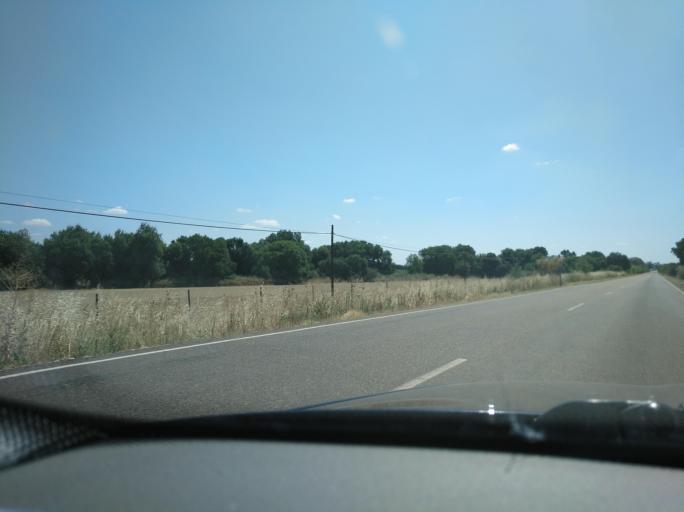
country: ES
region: Extremadura
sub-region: Provincia de Badajoz
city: Olivenza
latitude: 38.7197
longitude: -7.2038
